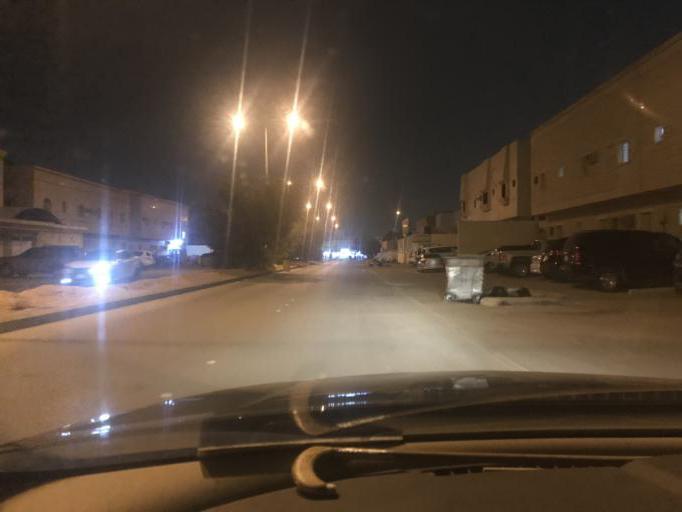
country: SA
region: Ar Riyad
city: Riyadh
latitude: 24.7519
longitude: 46.7781
